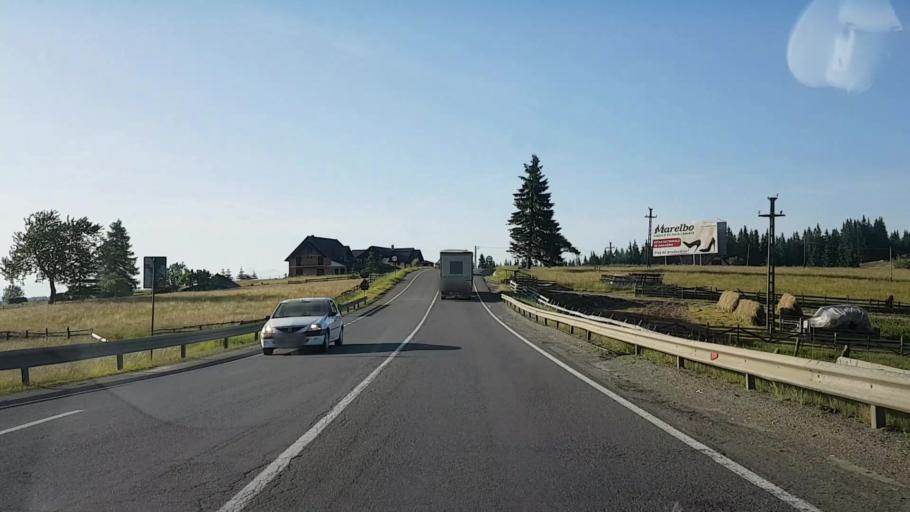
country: RO
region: Bistrita-Nasaud
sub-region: Comuna Lunca Ilvei
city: Lunca Ilvei
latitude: 47.2752
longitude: 25.0284
